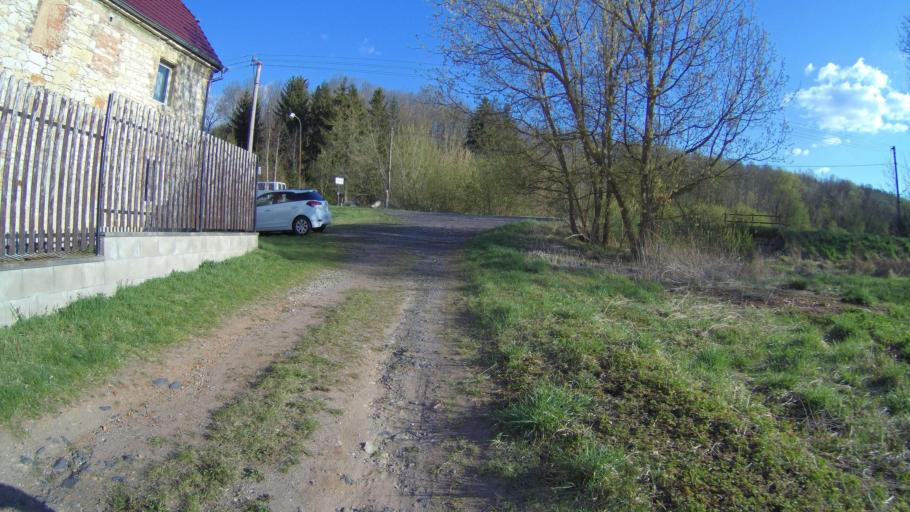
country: CZ
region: Ustecky
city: Zatec
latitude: 50.3049
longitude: 13.5967
